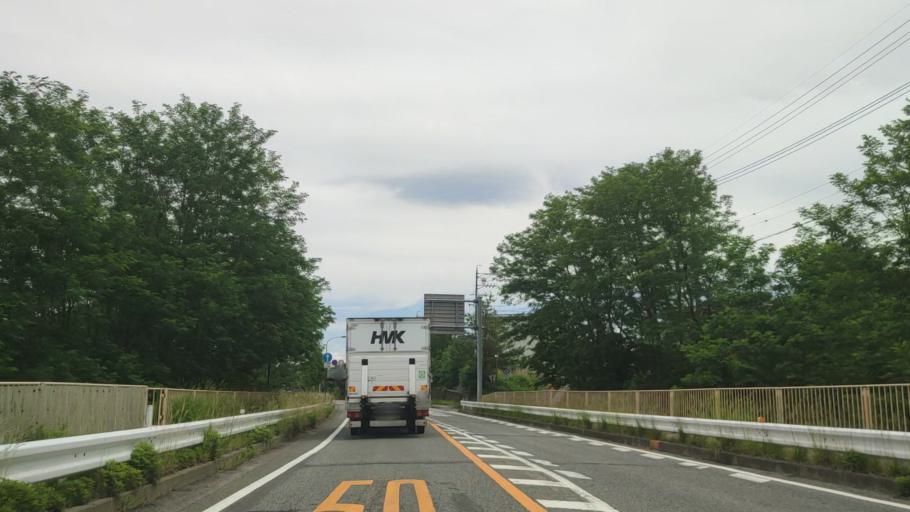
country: JP
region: Nagano
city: Komoro
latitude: 36.3153
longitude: 138.4454
